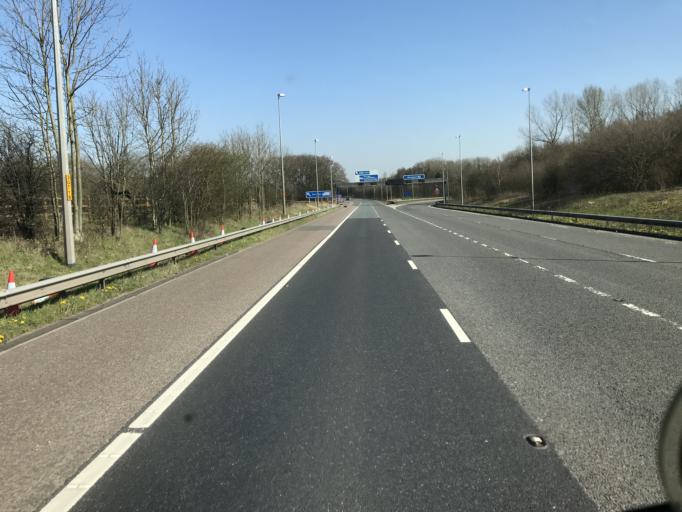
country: GB
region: England
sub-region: Warrington
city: Appleton Thorn
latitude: 53.3510
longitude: -2.5119
